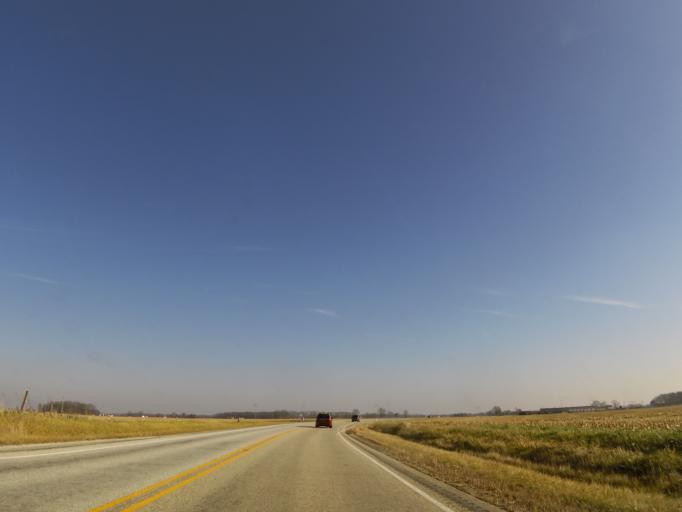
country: US
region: Indiana
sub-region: Shelby County
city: Morristown
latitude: 39.5723
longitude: -85.6127
